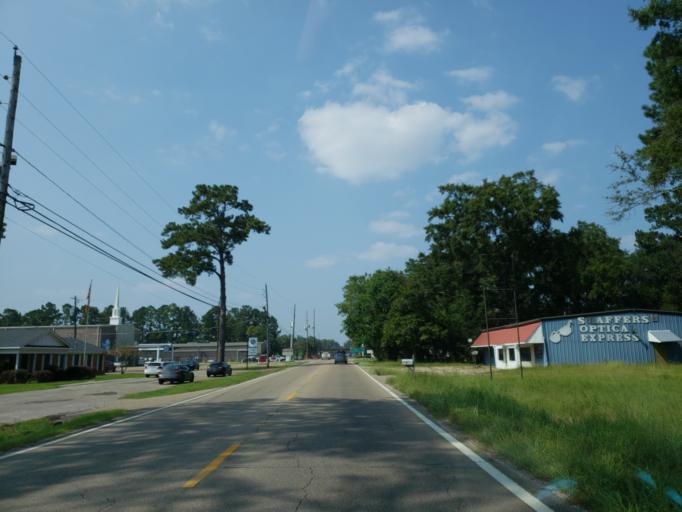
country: US
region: Mississippi
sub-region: Jones County
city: Ellisville
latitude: 31.6304
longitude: -89.1809
